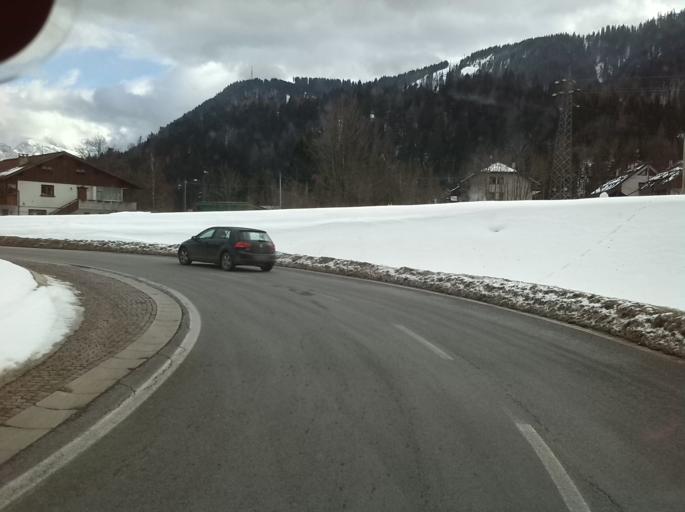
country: IT
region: Friuli Venezia Giulia
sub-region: Provincia di Udine
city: Tarvisio
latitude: 46.5077
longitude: 13.5431
